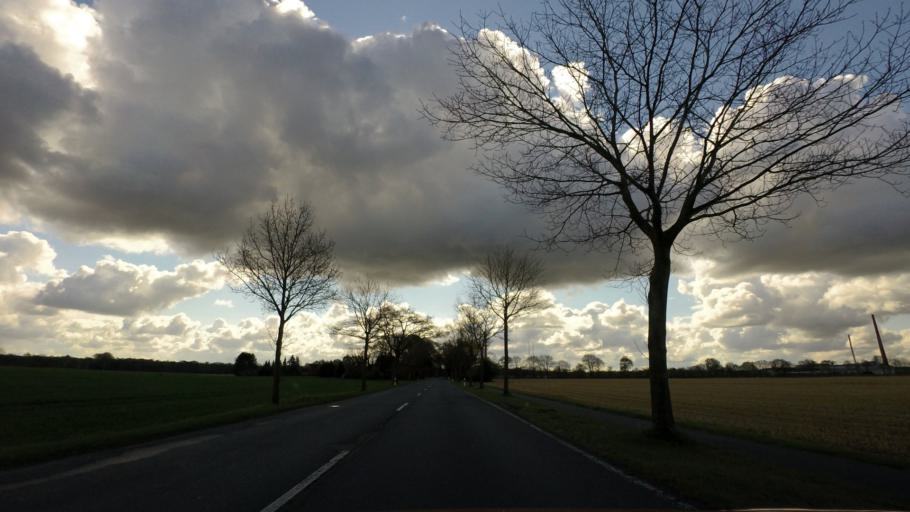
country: DE
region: Lower Saxony
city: Hatten
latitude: 53.0702
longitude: 8.4225
